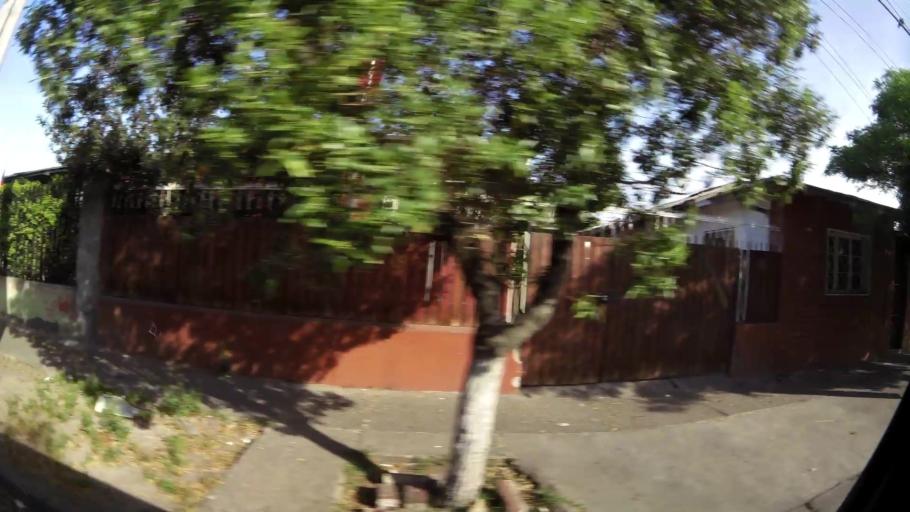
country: CL
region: Santiago Metropolitan
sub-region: Provincia de Santiago
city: Santiago
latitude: -33.5084
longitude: -70.6298
